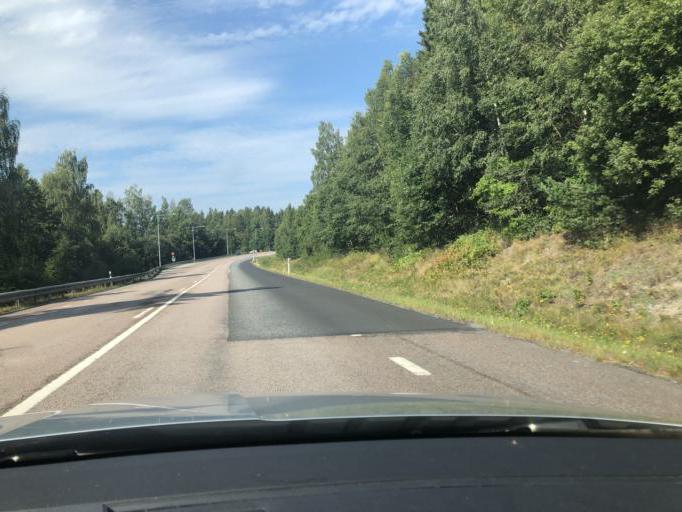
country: SE
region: Vaesternorrland
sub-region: Kramfors Kommun
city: Kramfors
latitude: 62.7978
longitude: 17.8776
